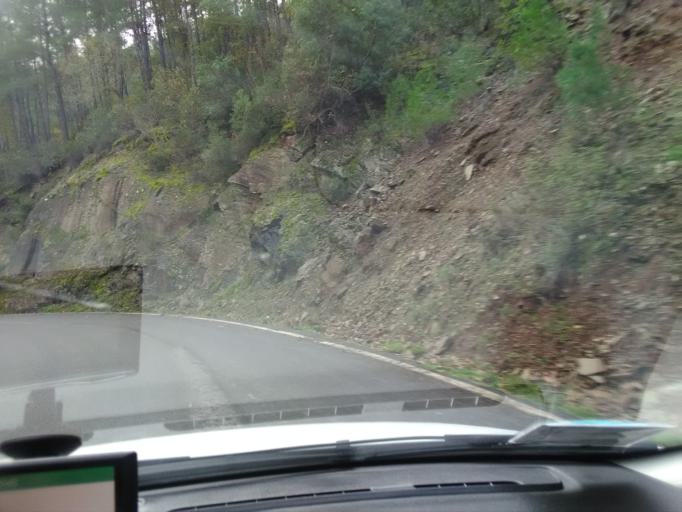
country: TR
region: Antalya
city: Gazipasa
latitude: 36.2459
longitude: 32.4114
